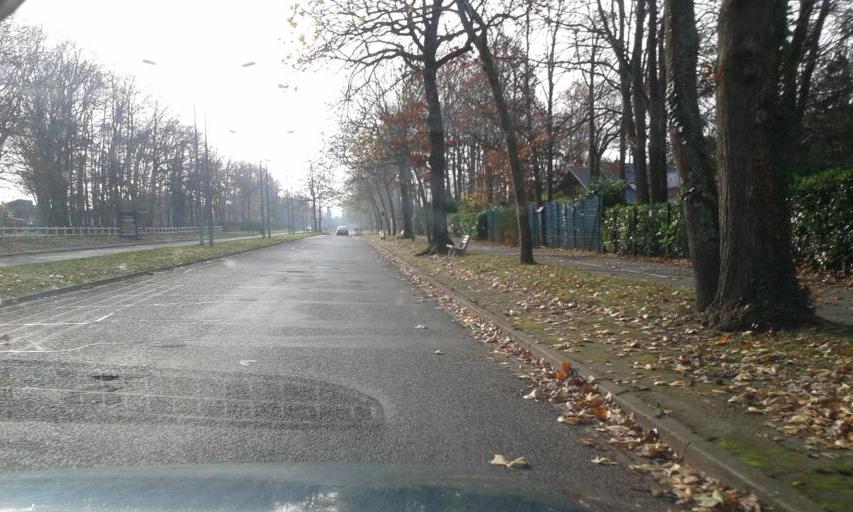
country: FR
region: Centre
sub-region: Departement du Loiret
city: Saint-Cyr-en-Val
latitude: 47.8219
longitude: 1.9311
